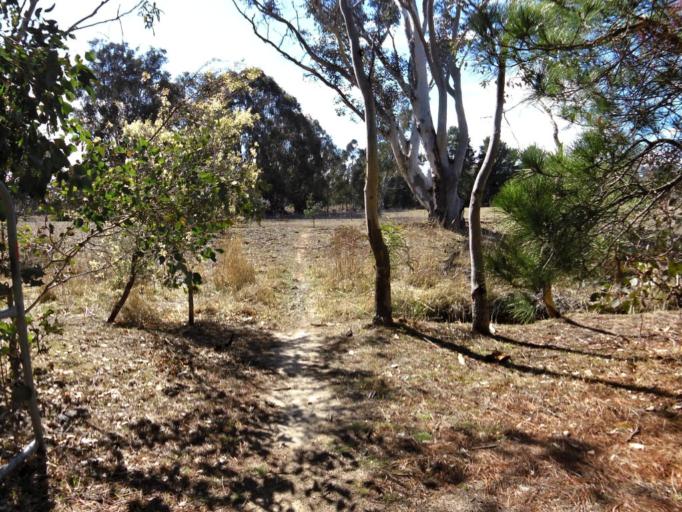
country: AU
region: Australian Capital Territory
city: Kaleen
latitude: -35.2080
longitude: 149.1944
